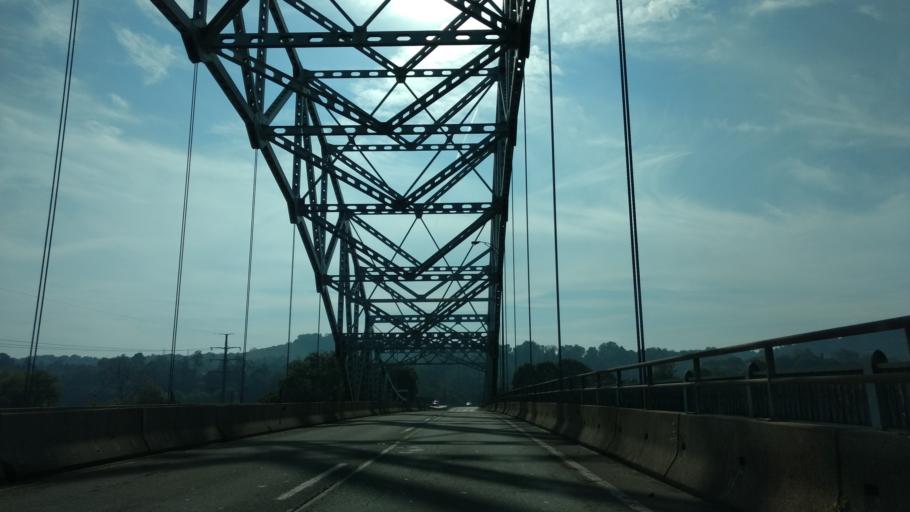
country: US
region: Pennsylvania
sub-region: Allegheny County
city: Elizabeth
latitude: 40.2751
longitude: -79.8883
